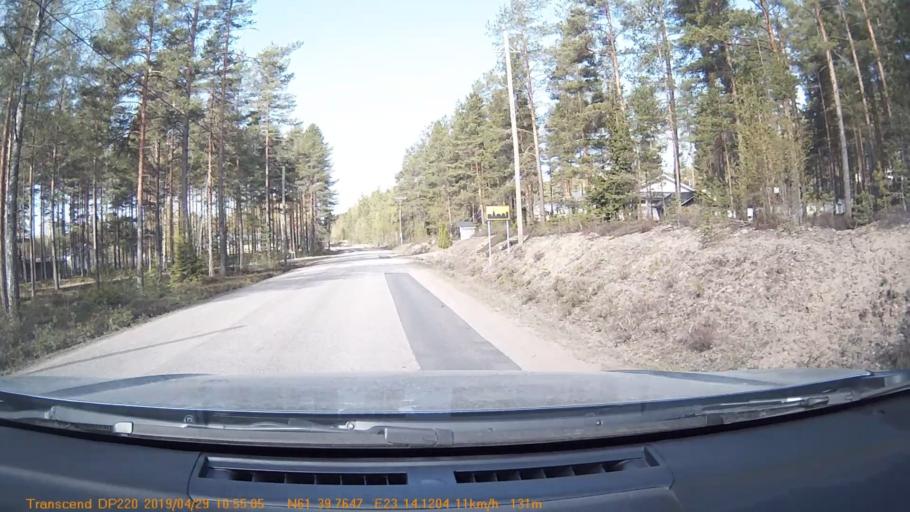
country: FI
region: Pirkanmaa
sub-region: Tampere
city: Haemeenkyroe
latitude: 61.6627
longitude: 23.2353
